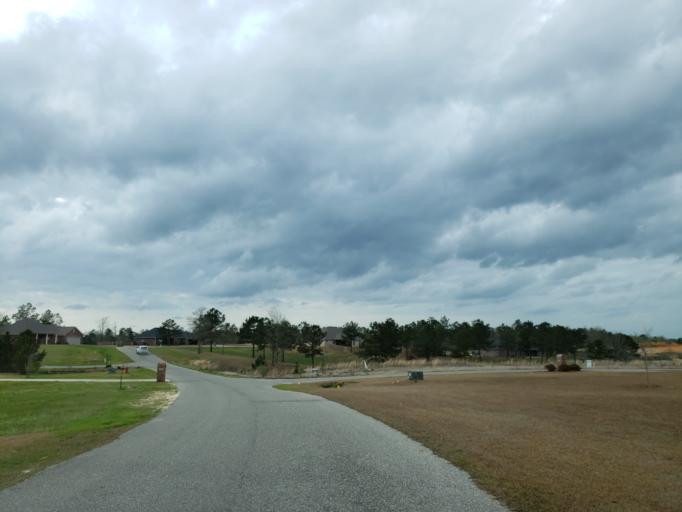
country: US
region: Mississippi
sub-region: Jones County
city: Ellisville
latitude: 31.5551
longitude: -89.2560
